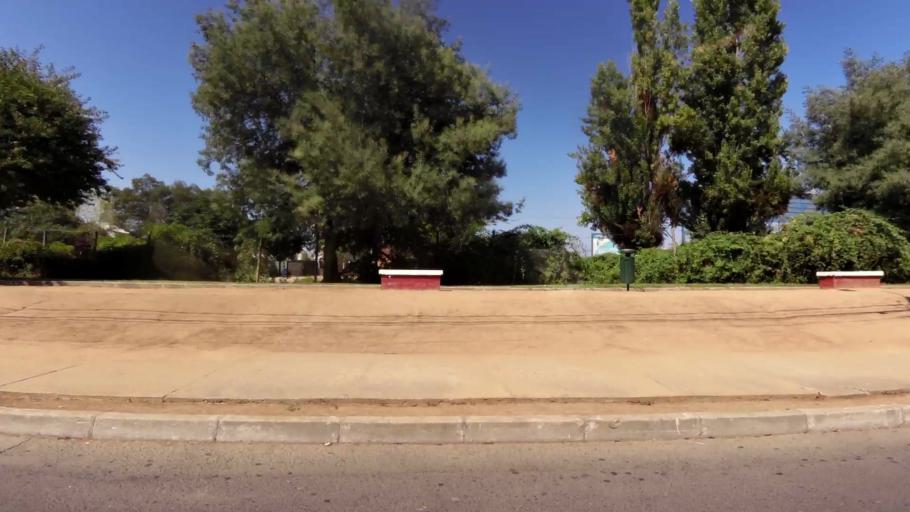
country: CL
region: Maule
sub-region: Provincia de Talca
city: Talca
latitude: -35.4132
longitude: -71.6469
